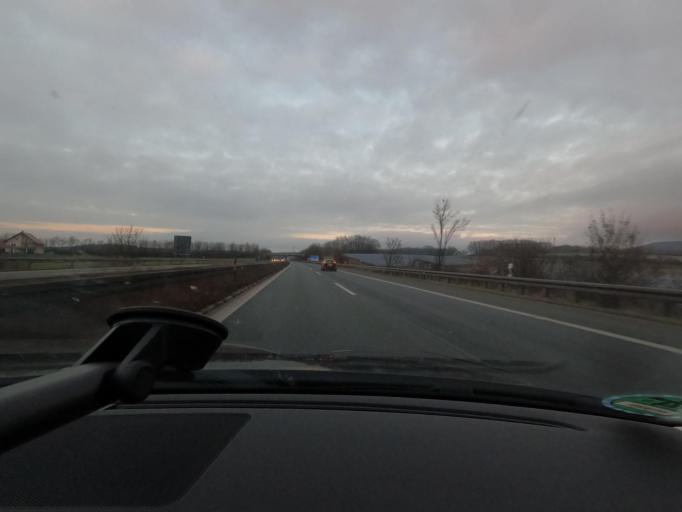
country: DE
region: Bavaria
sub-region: Upper Franconia
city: Hirschaid
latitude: 49.8271
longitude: 11.0084
